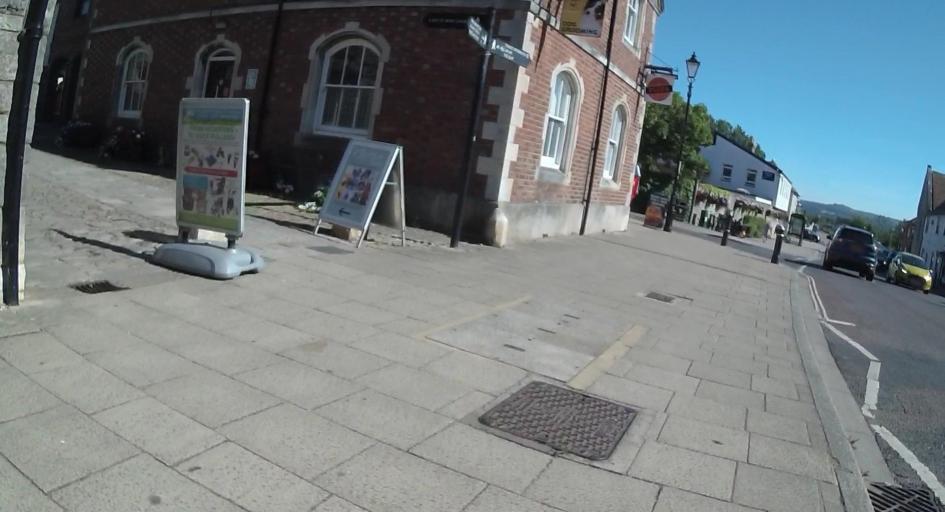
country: GB
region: England
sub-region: Dorset
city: Wareham
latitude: 50.6850
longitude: -2.1095
